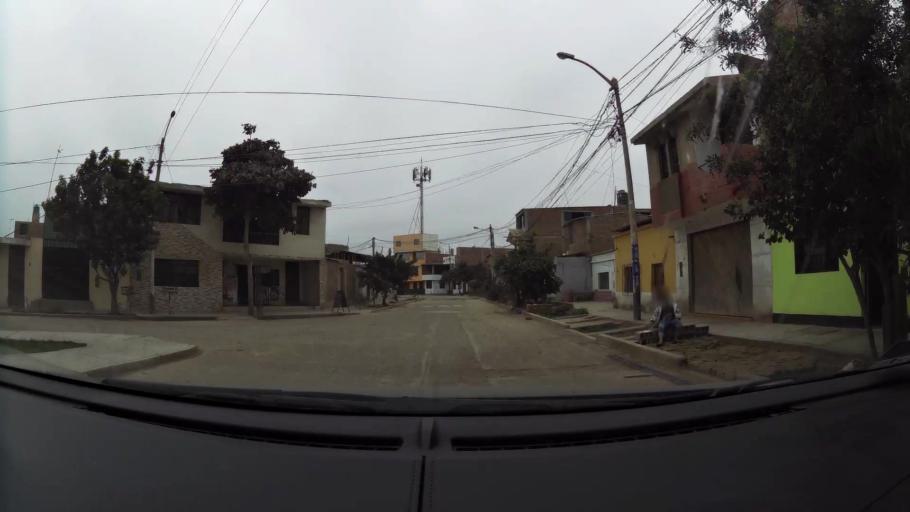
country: PE
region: La Libertad
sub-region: Provincia de Trujillo
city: Buenos Aires
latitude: -8.1423
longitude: -79.0490
